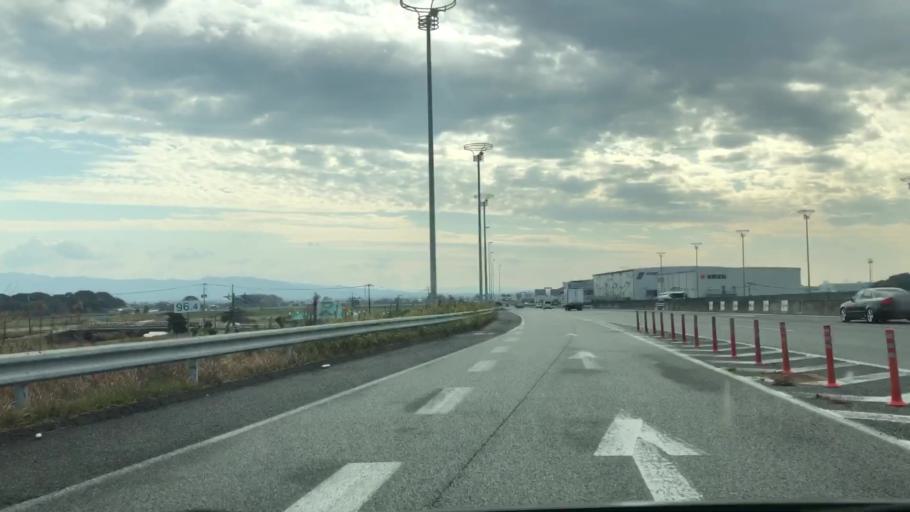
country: JP
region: Saga Prefecture
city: Tosu
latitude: 33.3940
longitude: 130.5385
